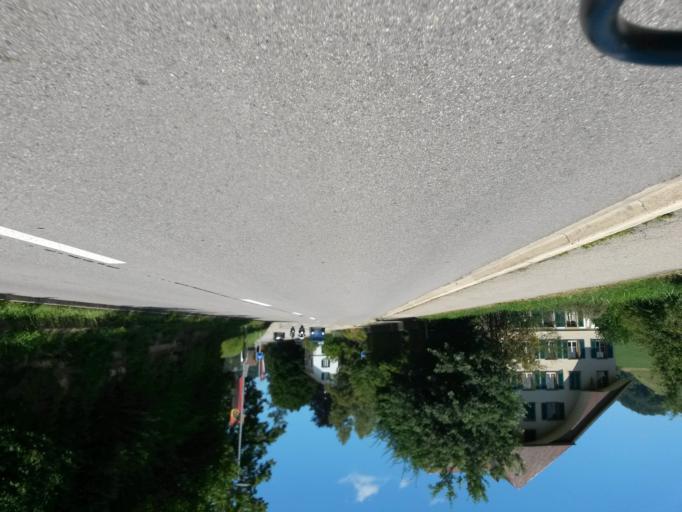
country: CH
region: Bern
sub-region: Bern-Mittelland District
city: Walkringen
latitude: 46.9446
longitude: 7.6183
